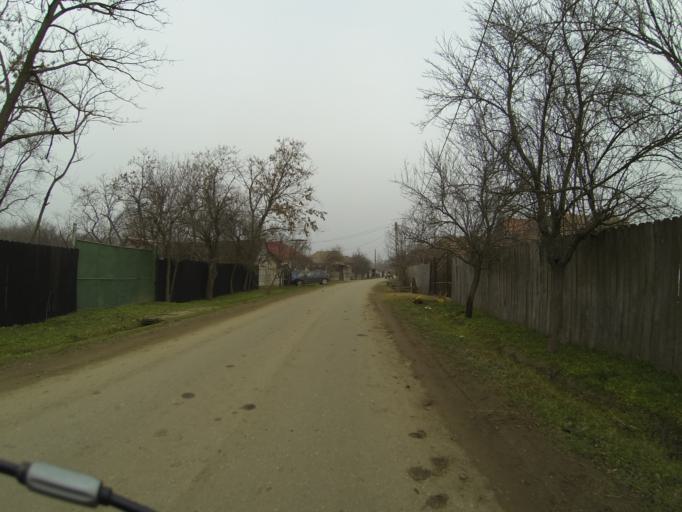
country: RO
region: Mehedinti
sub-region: Comuna Balacita
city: Gvardinita
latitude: 44.3966
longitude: 23.1446
